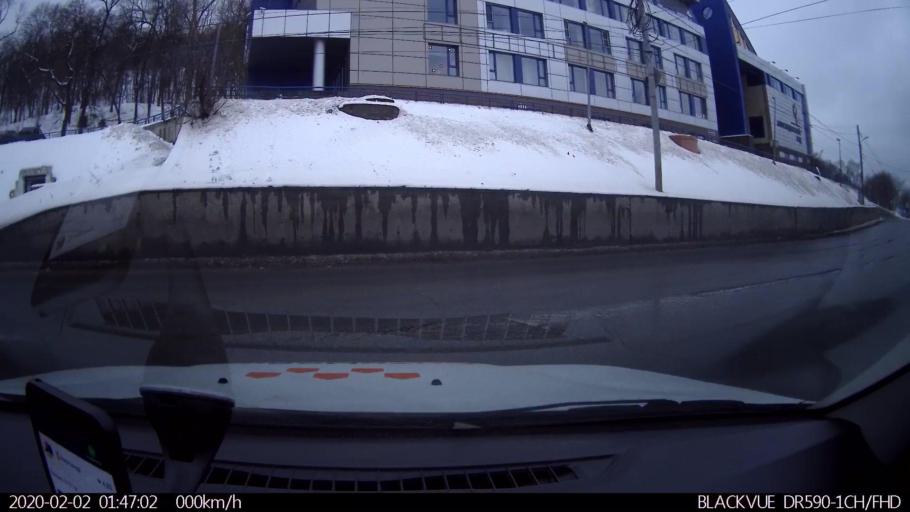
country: RU
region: Nizjnij Novgorod
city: Nizhniy Novgorod
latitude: 56.3342
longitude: 44.0269
